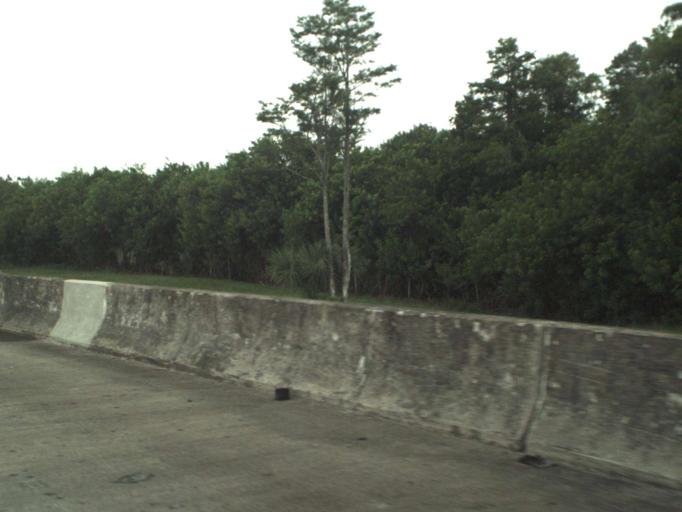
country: US
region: Florida
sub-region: Martin County
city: Port Salerno
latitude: 27.0591
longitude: -80.2390
